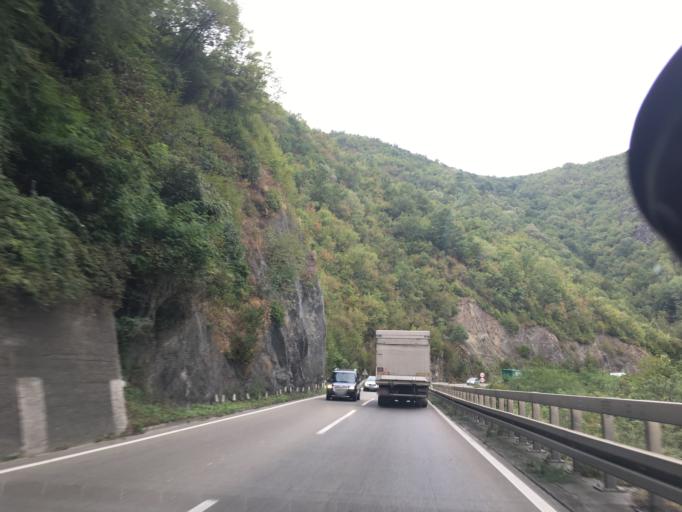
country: RS
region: Central Serbia
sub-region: Moravicki Okrug
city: Lucani
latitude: 43.9065
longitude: 20.2346
